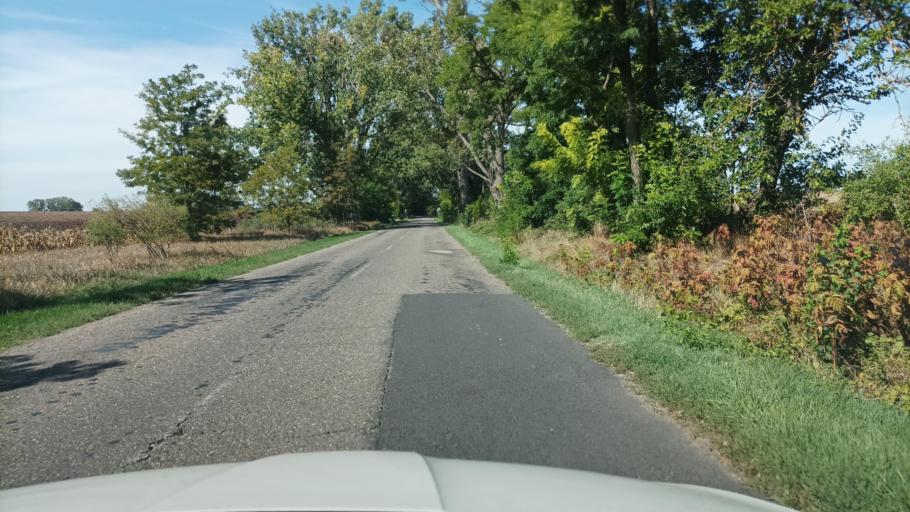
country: HU
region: Pest
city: Zsambok
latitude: 47.5528
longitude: 19.5792
